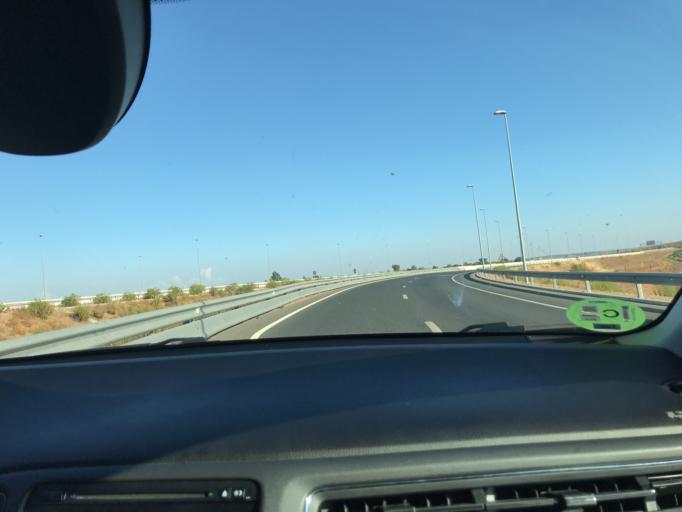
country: ES
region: Andalusia
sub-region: Provincia de Sevilla
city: Alcala de Guadaira
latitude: 37.4293
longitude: -5.8437
